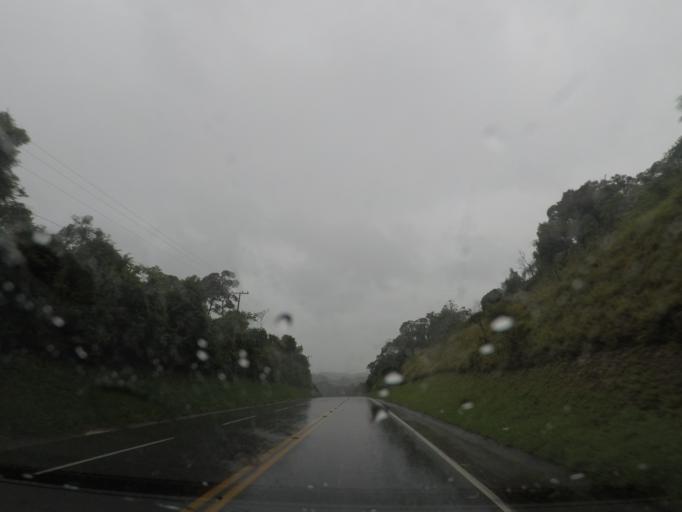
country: BR
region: Parana
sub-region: Almirante Tamandare
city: Almirante Tamandare
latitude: -25.3653
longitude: -49.3212
